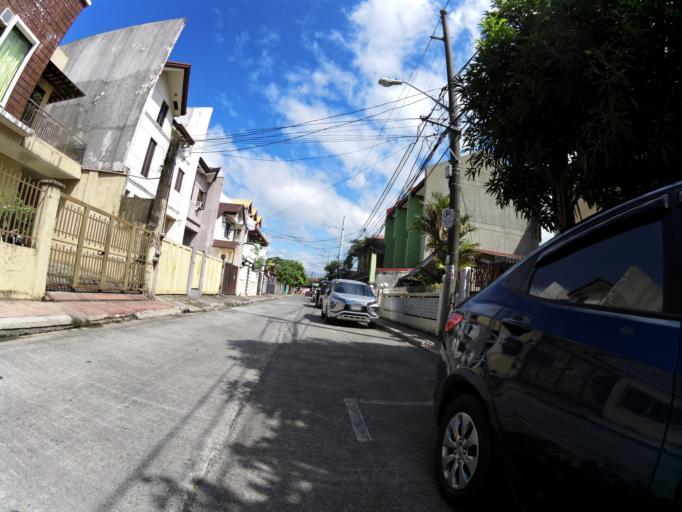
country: PH
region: Calabarzon
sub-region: Province of Rizal
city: Antipolo
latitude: 14.6404
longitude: 121.1127
